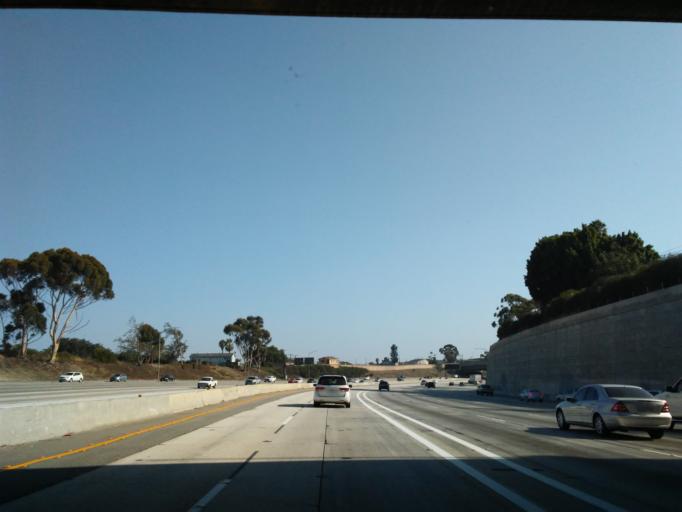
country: US
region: California
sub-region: Los Angeles County
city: West Athens
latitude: 33.9238
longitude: -118.2814
